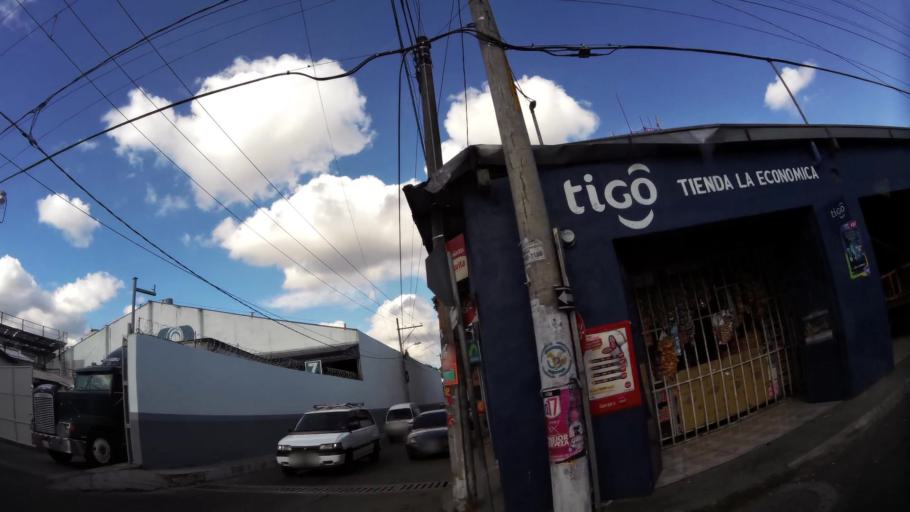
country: GT
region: Guatemala
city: Villa Nueva
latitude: 14.5289
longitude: -90.5885
